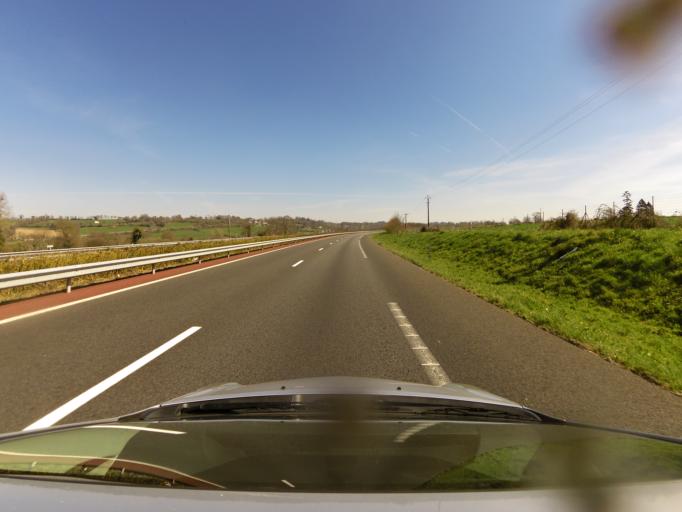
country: FR
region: Lower Normandy
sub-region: Departement de la Manche
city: Saint-Senier-sous-Avranches
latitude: 48.7219
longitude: -1.3154
